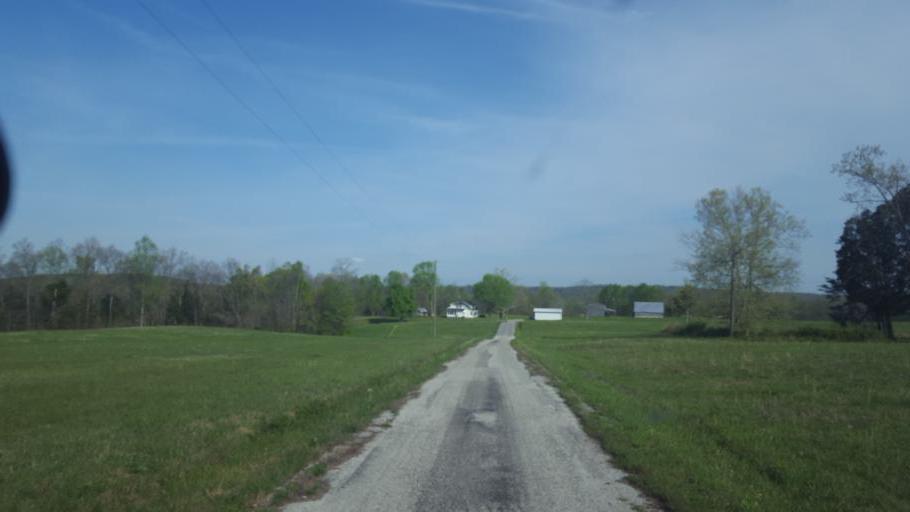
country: US
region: Kentucky
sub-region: Edmonson County
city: Brownsville
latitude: 37.3321
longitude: -86.1129
